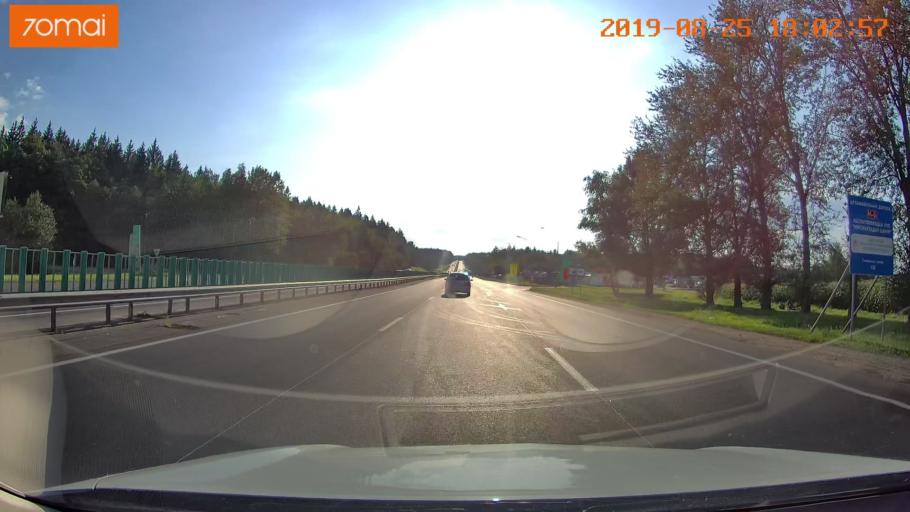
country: BY
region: Minsk
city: Zhdanovichy
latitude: 53.9118
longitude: 27.4016
